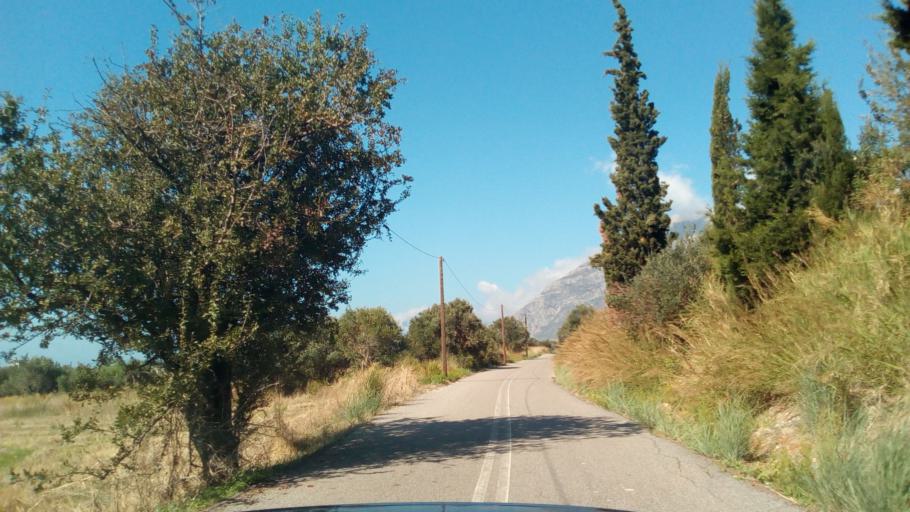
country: GR
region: West Greece
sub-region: Nomos Aitolias kai Akarnanias
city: Antirrio
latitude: 38.3384
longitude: 21.7391
